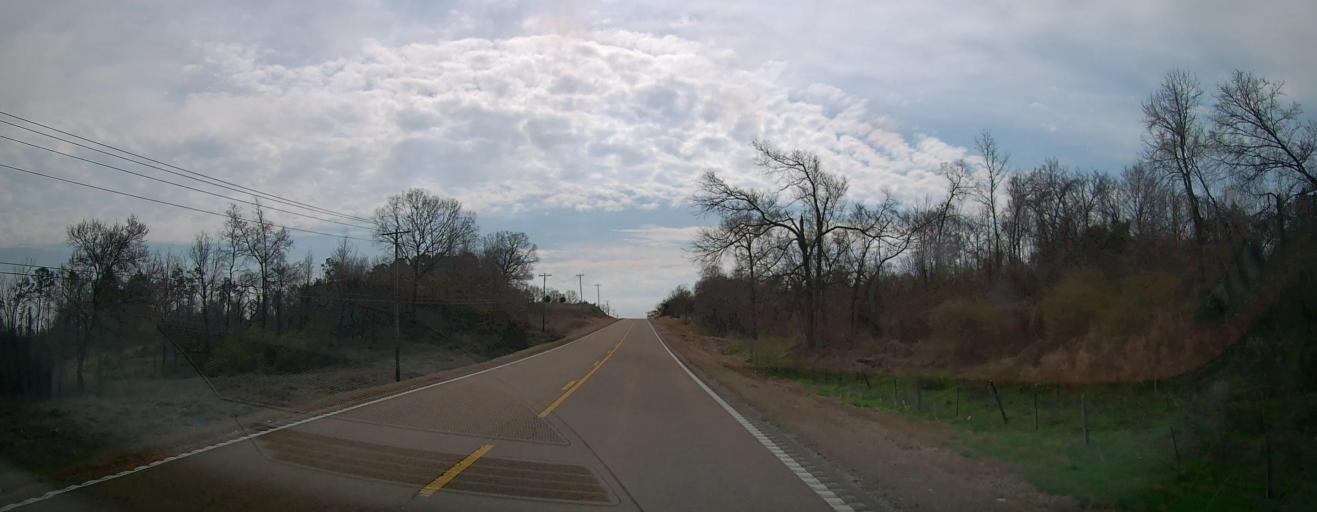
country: US
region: Mississippi
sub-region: Marshall County
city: Holly Springs
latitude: 34.7417
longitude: -89.4253
